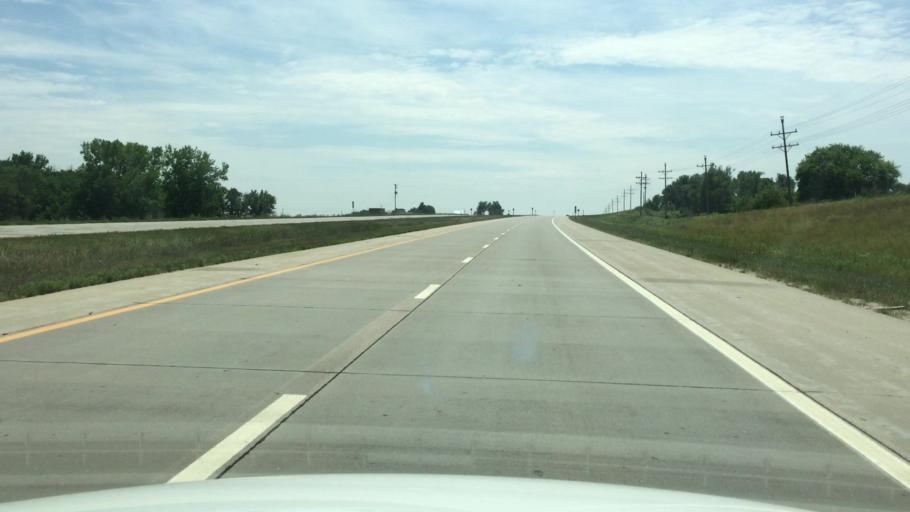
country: US
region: Kansas
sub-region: Jackson County
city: Holton
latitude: 39.2834
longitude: -95.7194
